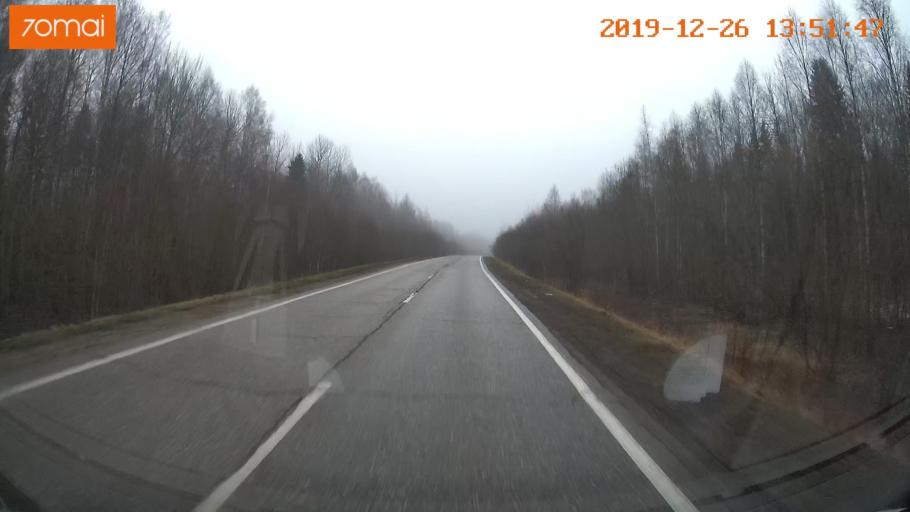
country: RU
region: Jaroslavl
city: Poshekhon'ye
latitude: 58.6398
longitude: 38.5949
